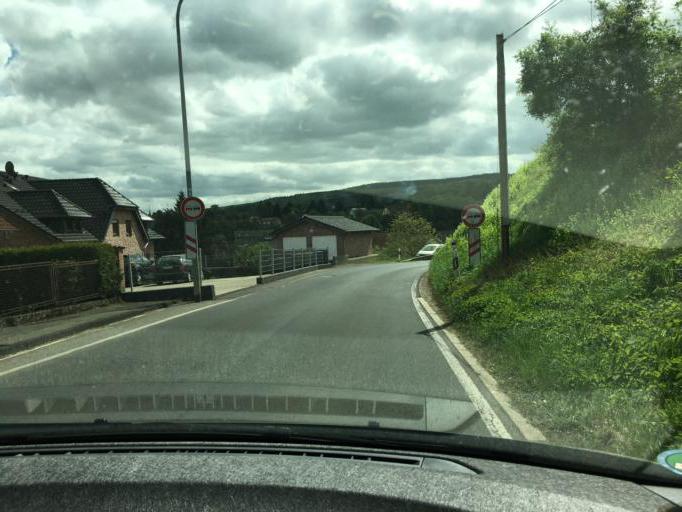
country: DE
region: North Rhine-Westphalia
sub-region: Regierungsbezirk Koln
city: Bad Munstereifel
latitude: 50.5833
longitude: 6.7670
